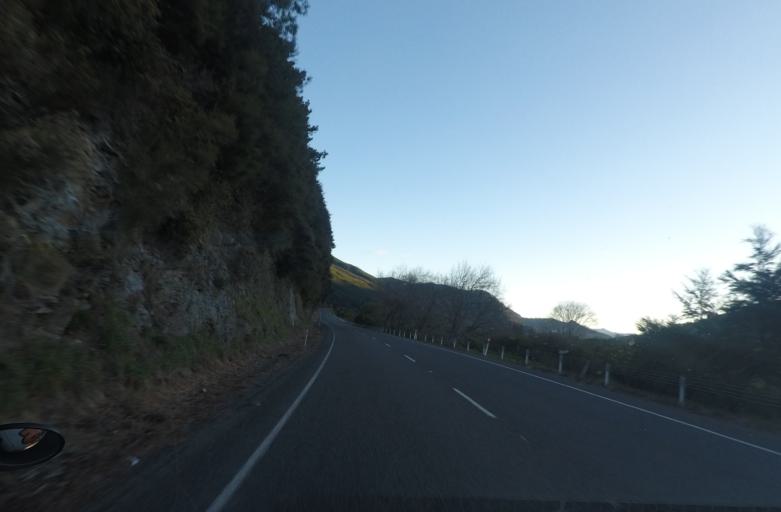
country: NZ
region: Marlborough
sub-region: Marlborough District
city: Picton
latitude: -41.2757
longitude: 173.7316
